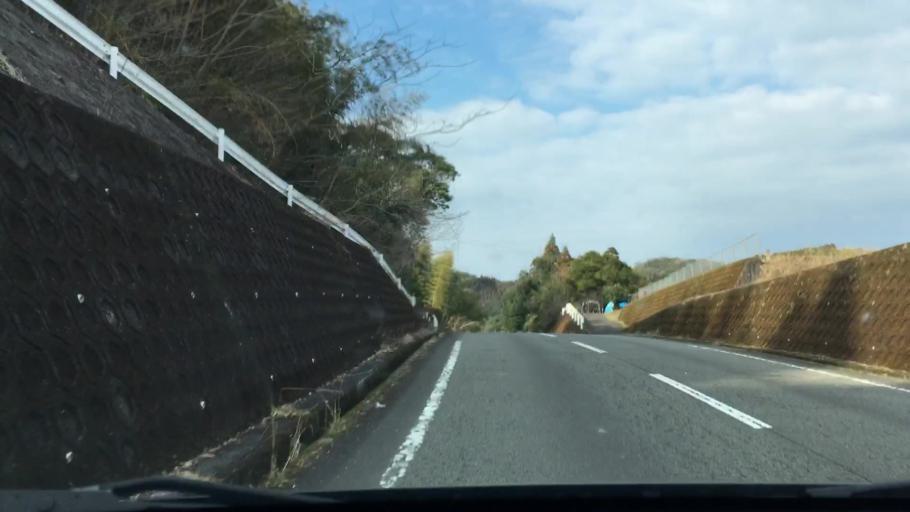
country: JP
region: Miyazaki
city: Nichinan
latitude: 31.5921
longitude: 131.3073
